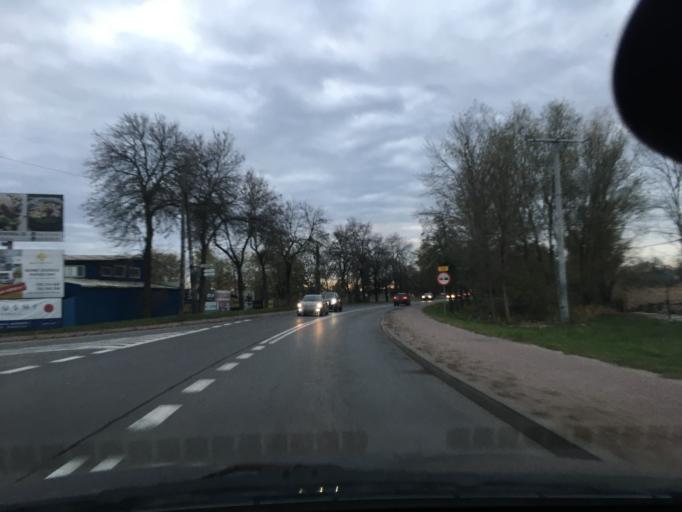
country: PL
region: Masovian Voivodeship
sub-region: Powiat piaseczynski
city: Lesznowola
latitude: 52.0906
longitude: 20.9346
